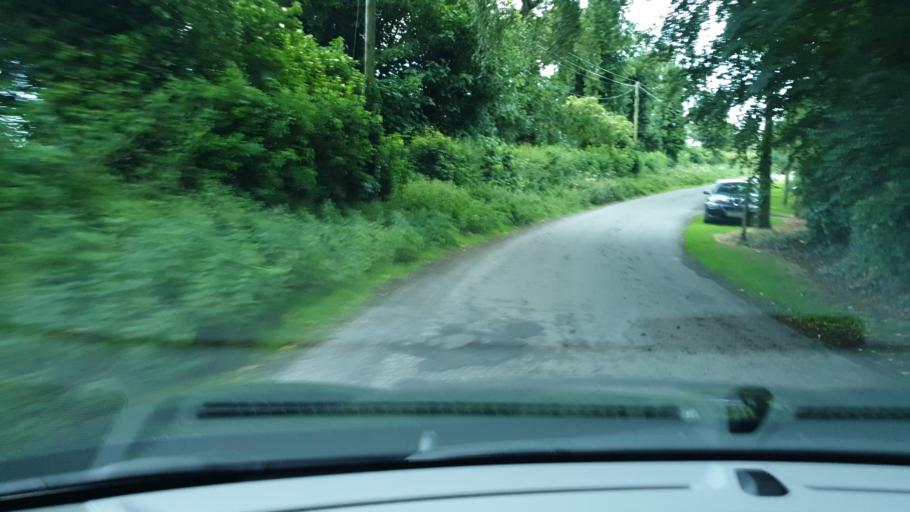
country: IE
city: Kentstown
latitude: 53.5903
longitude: -6.5653
